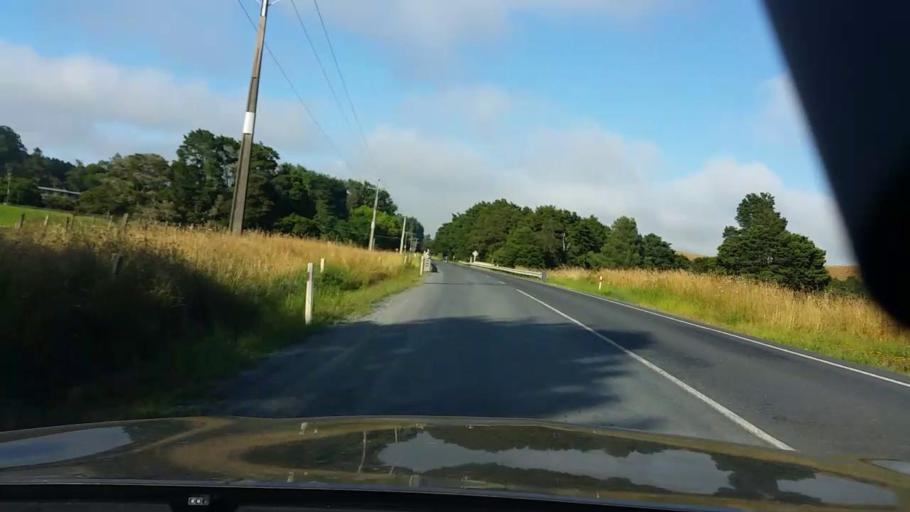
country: NZ
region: Waikato
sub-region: Hamilton City
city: Hamilton
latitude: -37.5939
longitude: 175.3628
